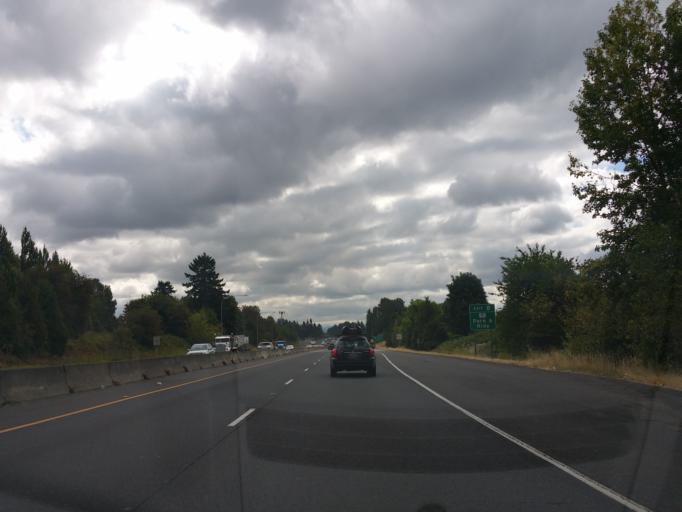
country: US
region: Washington
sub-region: Clark County
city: Mill Plain
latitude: 45.5950
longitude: -122.5160
